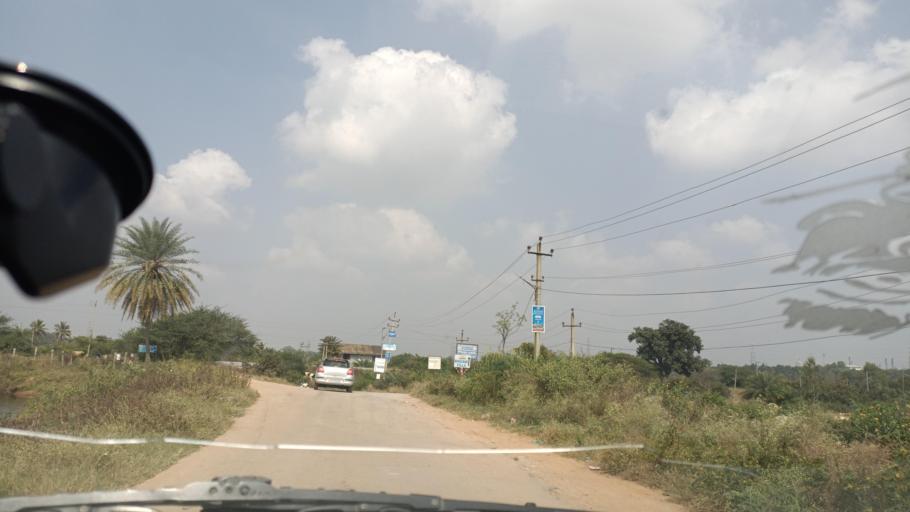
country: IN
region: Karnataka
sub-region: Bangalore Urban
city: Yelahanka
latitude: 13.1778
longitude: 77.6314
